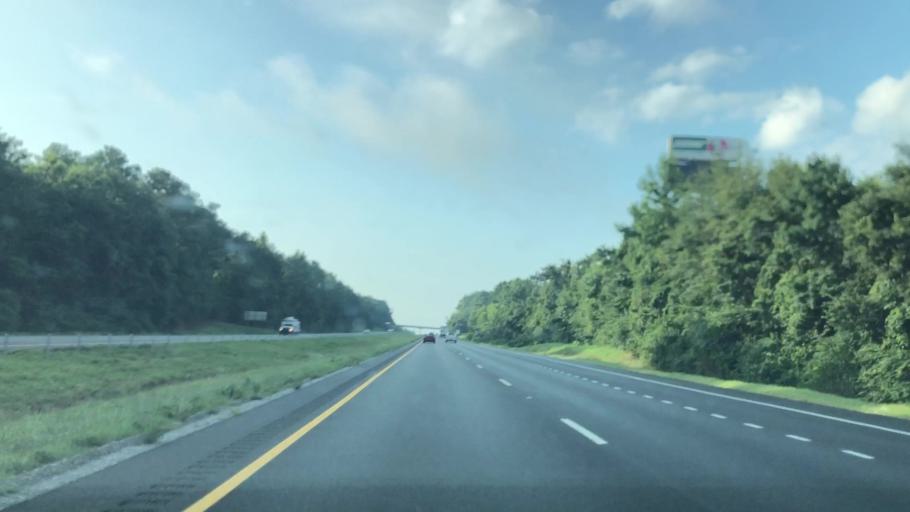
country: US
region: Alabama
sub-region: Chilton County
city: Clanton
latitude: 32.8391
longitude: -86.5938
